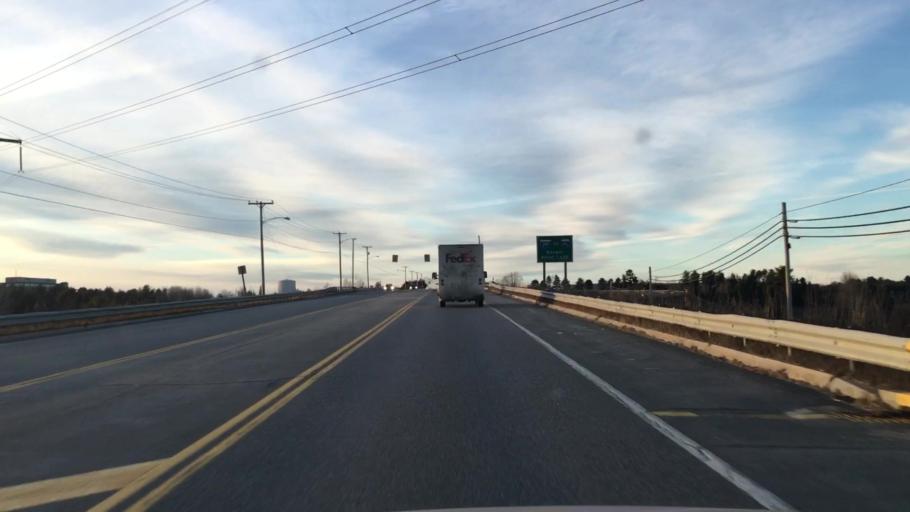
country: US
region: Maine
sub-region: Penobscot County
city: Holden
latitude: 44.7691
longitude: -68.7162
